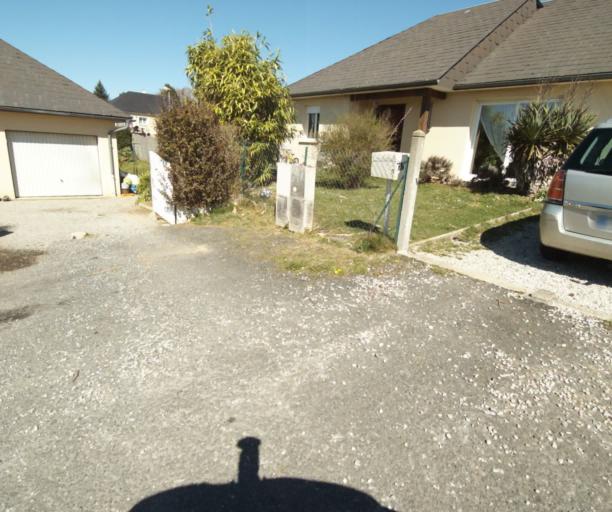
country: FR
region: Limousin
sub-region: Departement de la Correze
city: Seilhac
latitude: 45.3718
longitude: 1.7018
